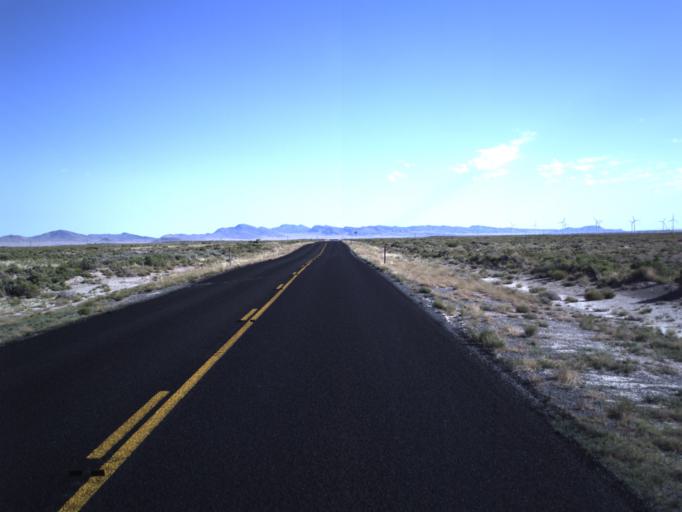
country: US
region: Utah
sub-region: Beaver County
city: Milford
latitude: 38.5283
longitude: -112.9911
